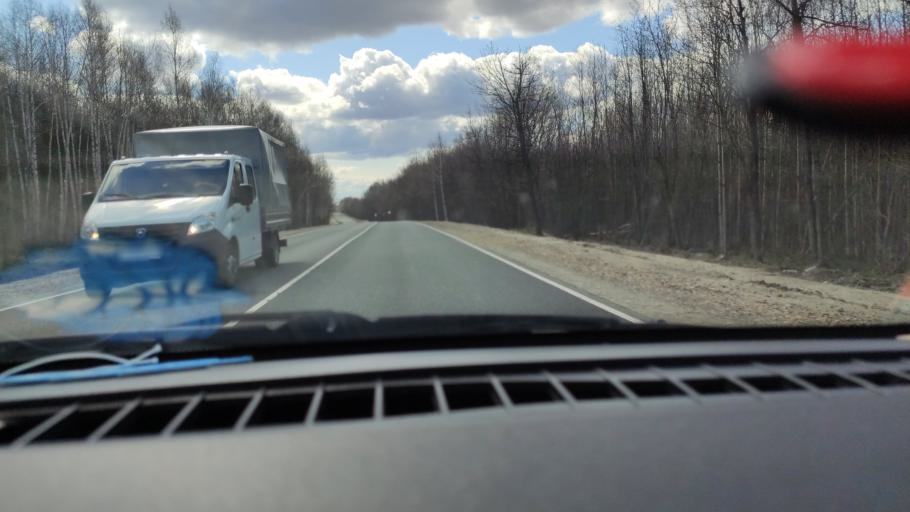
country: RU
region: Saratov
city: Khvalynsk
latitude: 52.4695
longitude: 48.0161
